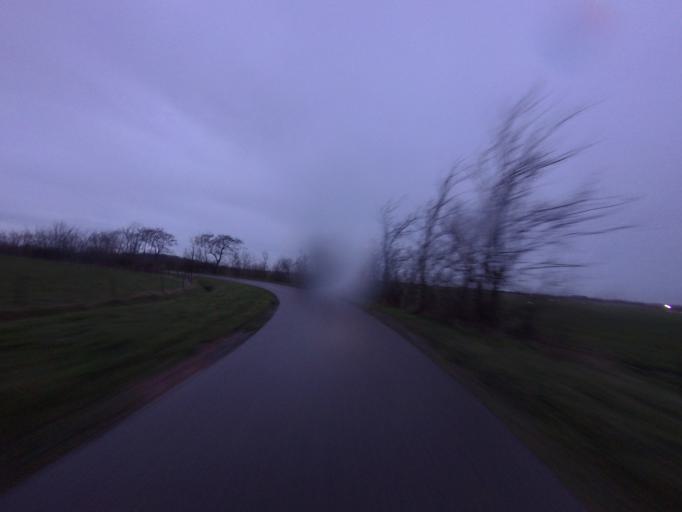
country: NL
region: North Holland
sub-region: Gemeente Texel
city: Den Burg
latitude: 53.0669
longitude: 4.8005
